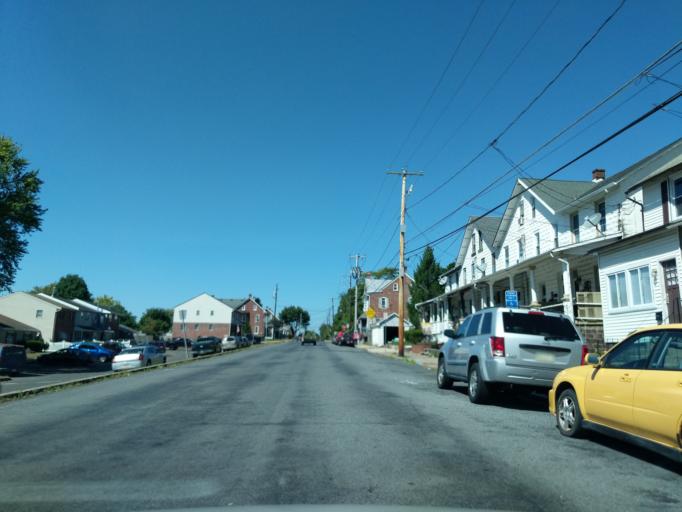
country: US
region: Pennsylvania
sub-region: Montgomery County
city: East Greenville
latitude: 40.4034
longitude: -75.5079
